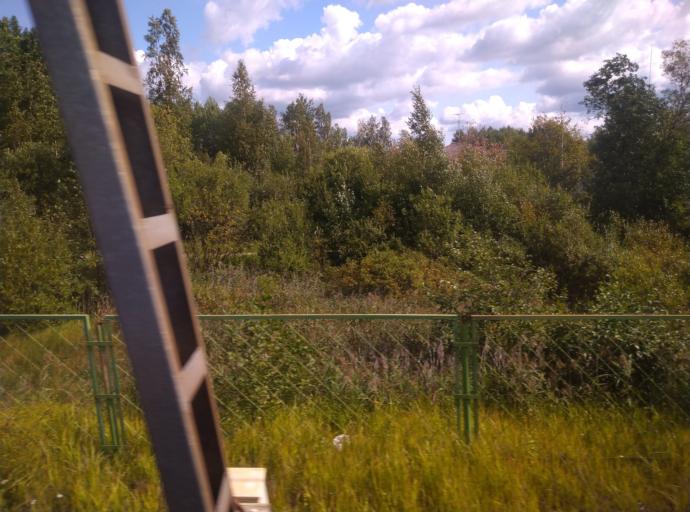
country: RU
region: Leningrad
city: Krasnyy Bor
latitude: 59.6773
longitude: 30.7055
